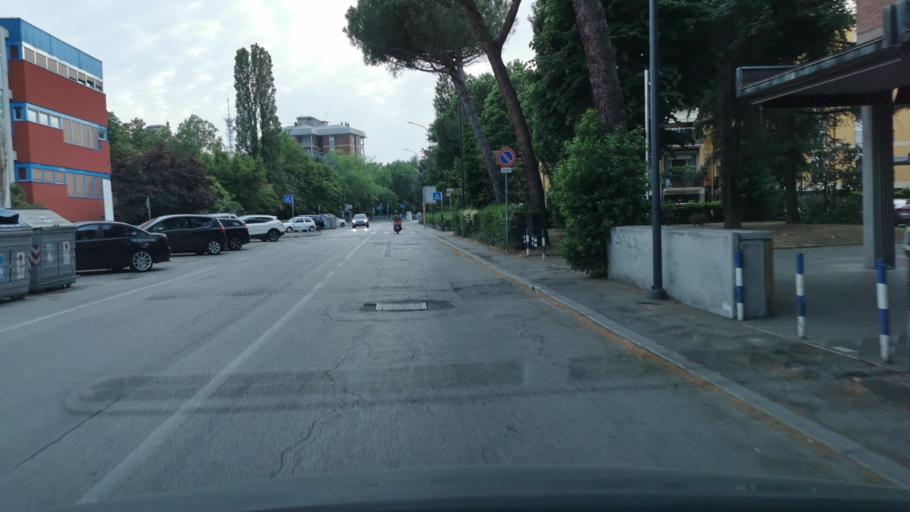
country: IT
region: Emilia-Romagna
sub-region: Provincia di Ravenna
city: Ravenna
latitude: 44.4074
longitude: 12.1935
